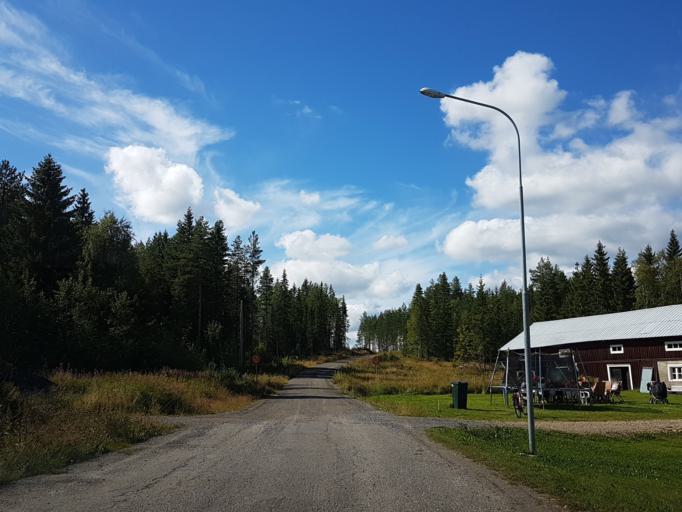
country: SE
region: Vaesterbotten
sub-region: Skelleftea Kommun
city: Burtraesk
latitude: 64.2717
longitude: 20.4897
